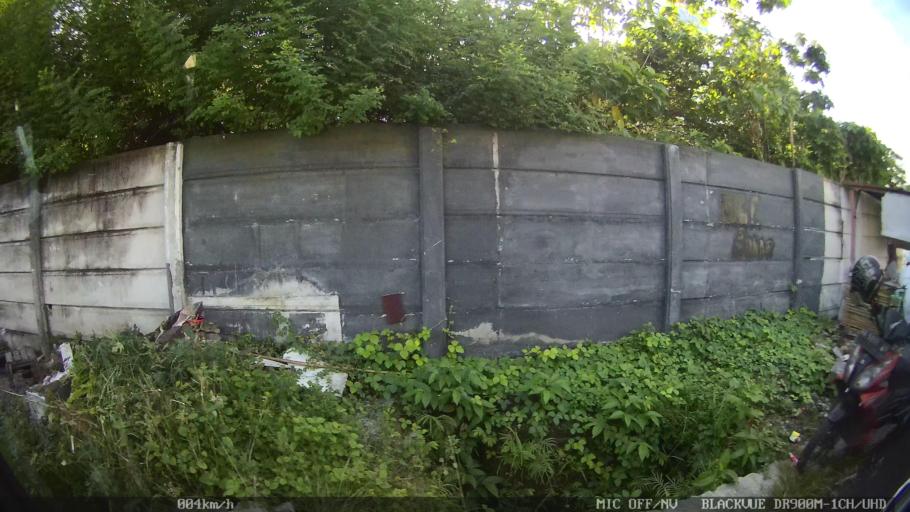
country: ID
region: North Sumatra
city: Medan
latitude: 3.5954
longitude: 98.6716
